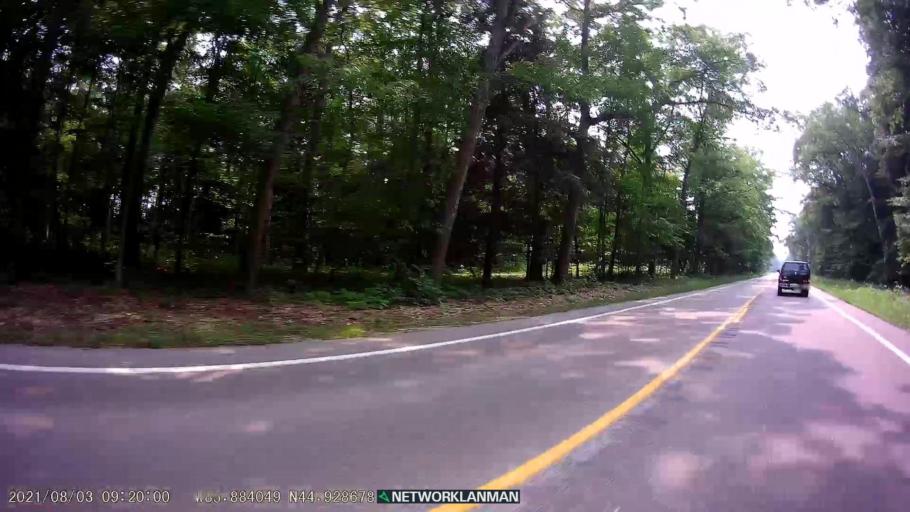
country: US
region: Michigan
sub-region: Leelanau County
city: Leland
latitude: 44.9284
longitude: -85.8838
